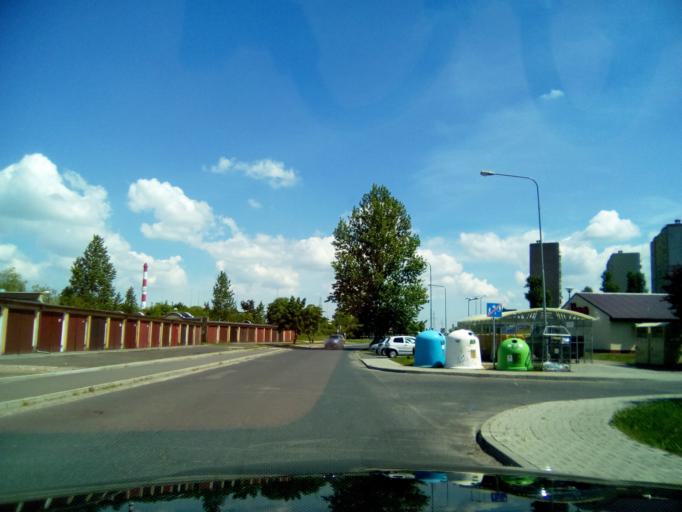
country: PL
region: Greater Poland Voivodeship
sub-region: Powiat gnieznienski
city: Gniezno
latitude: 52.5530
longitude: 17.6028
